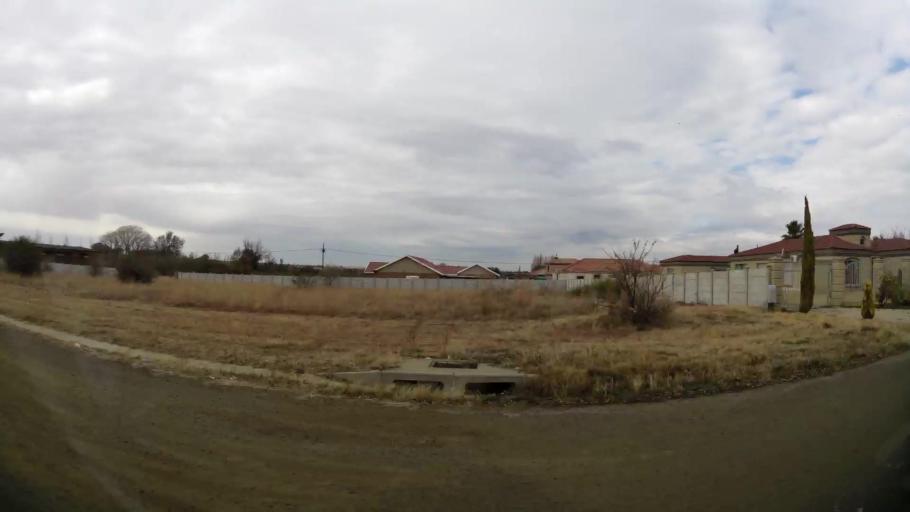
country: ZA
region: Orange Free State
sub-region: Fezile Dabi District Municipality
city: Kroonstad
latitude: -27.6307
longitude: 27.2451
